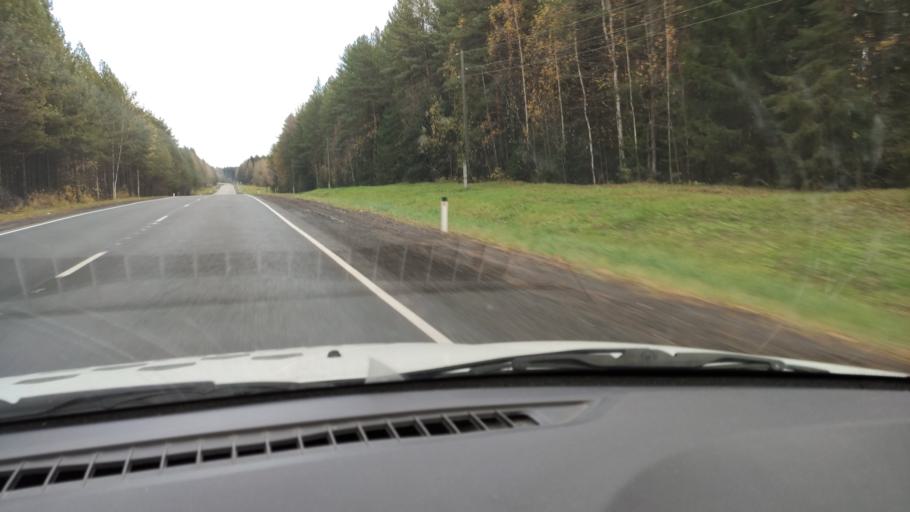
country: RU
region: Kirov
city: Belaya Kholunitsa
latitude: 58.8952
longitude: 50.9013
